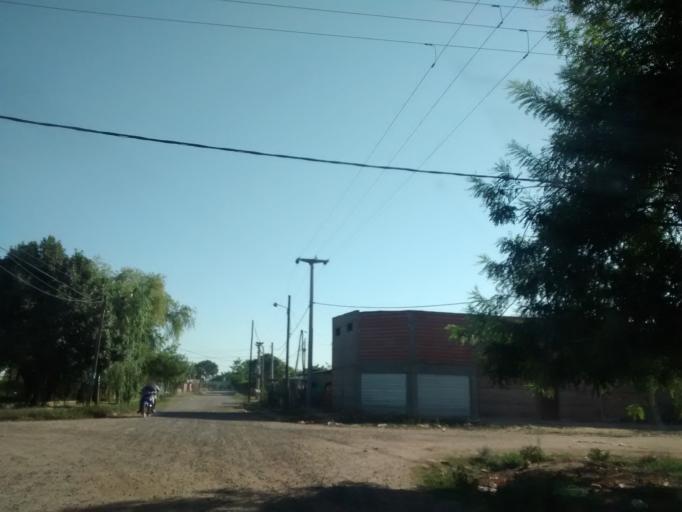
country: AR
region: Chaco
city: Resistencia
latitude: -27.4609
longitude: -58.9614
